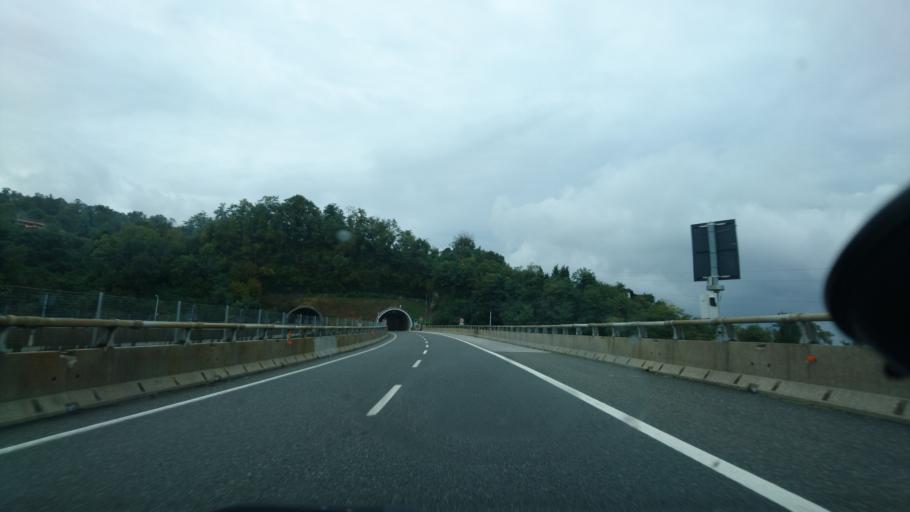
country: IT
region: Piedmont
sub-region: Provincia di Novara
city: Nebbiuno
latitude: 45.8102
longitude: 8.5351
